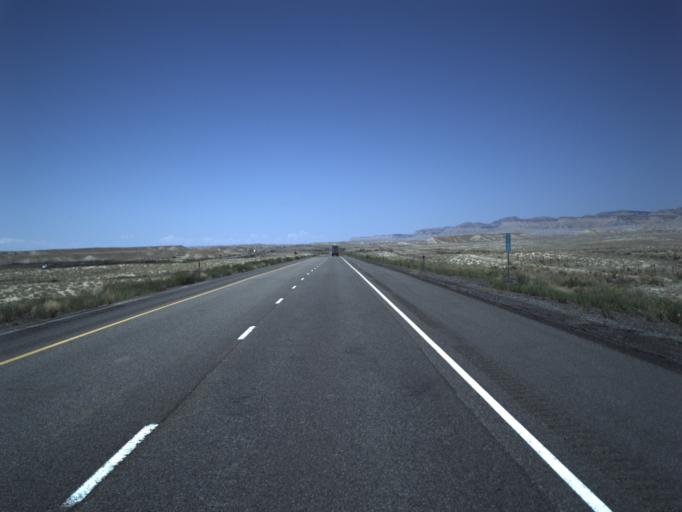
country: US
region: Utah
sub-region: Grand County
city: Moab
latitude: 38.9390
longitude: -109.4928
